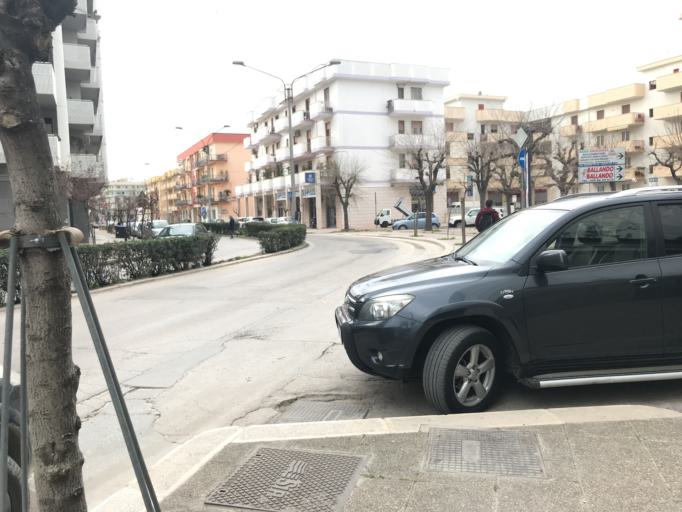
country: IT
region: Apulia
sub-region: Provincia di Bari
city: Corato
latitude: 41.1574
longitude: 16.4153
